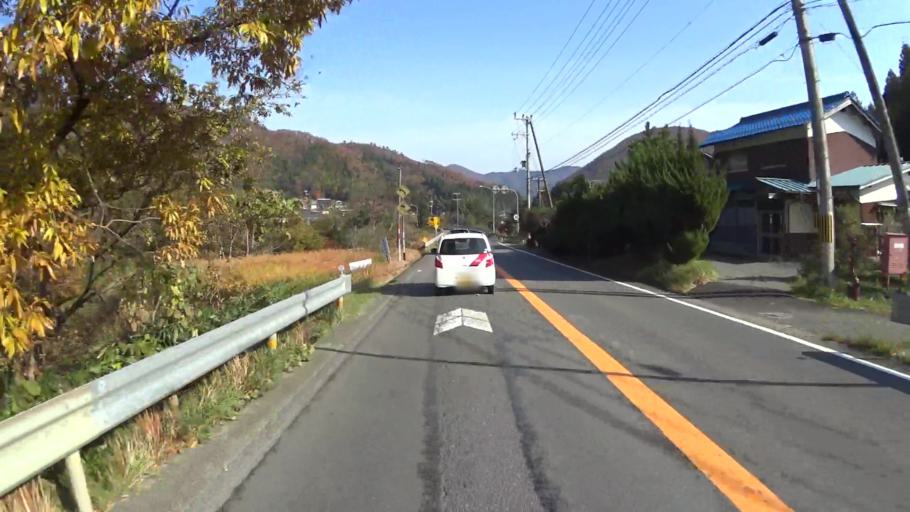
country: JP
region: Kyoto
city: Ayabe
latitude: 35.2053
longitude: 135.2834
